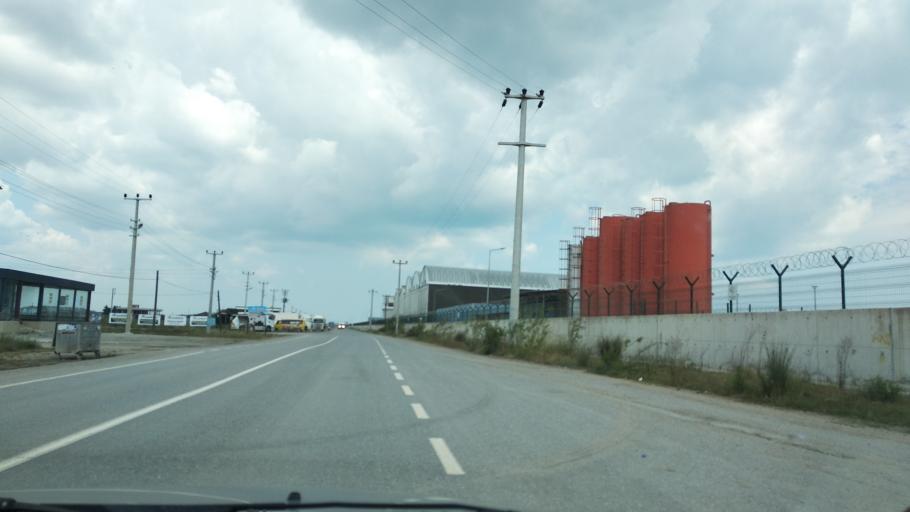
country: TR
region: Sakarya
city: Karasu
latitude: 41.1166
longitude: 30.6754
